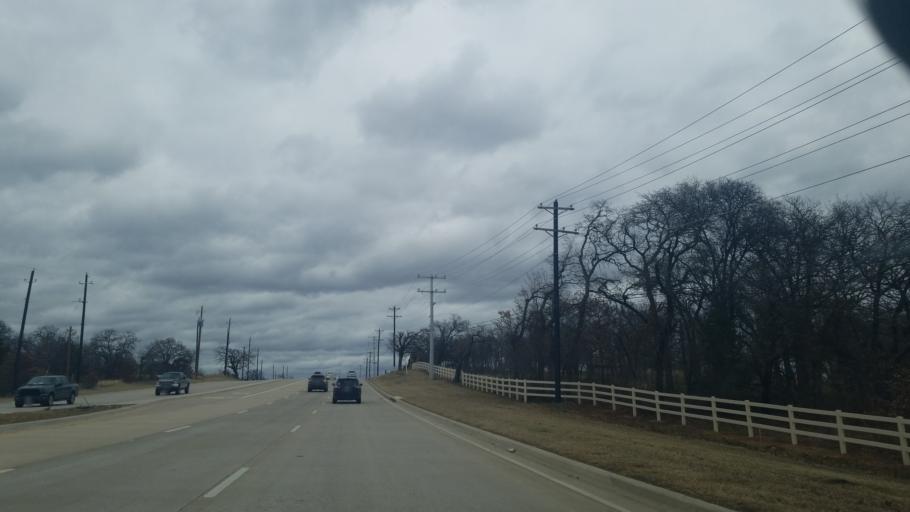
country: US
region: Texas
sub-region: Denton County
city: Bartonville
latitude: 33.0434
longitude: -97.1580
